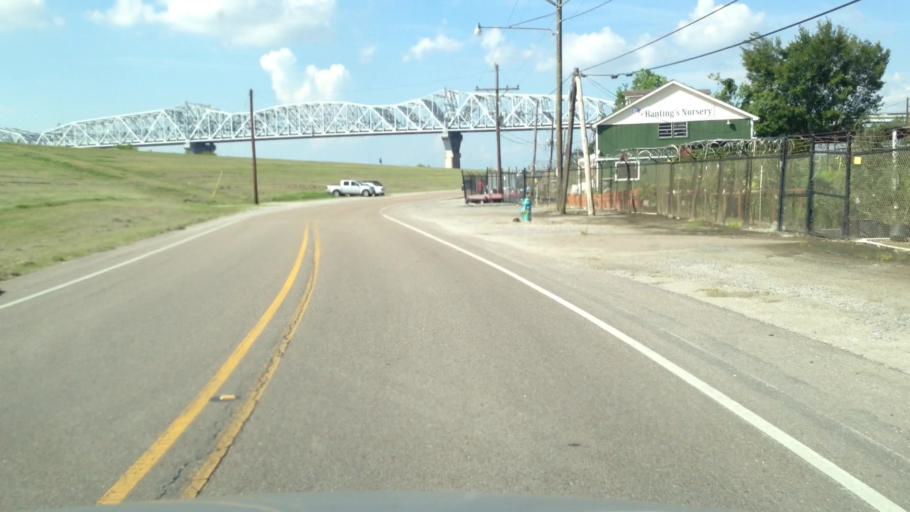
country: US
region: Louisiana
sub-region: Jefferson Parish
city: Bridge City
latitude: 29.9357
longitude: -90.1711
